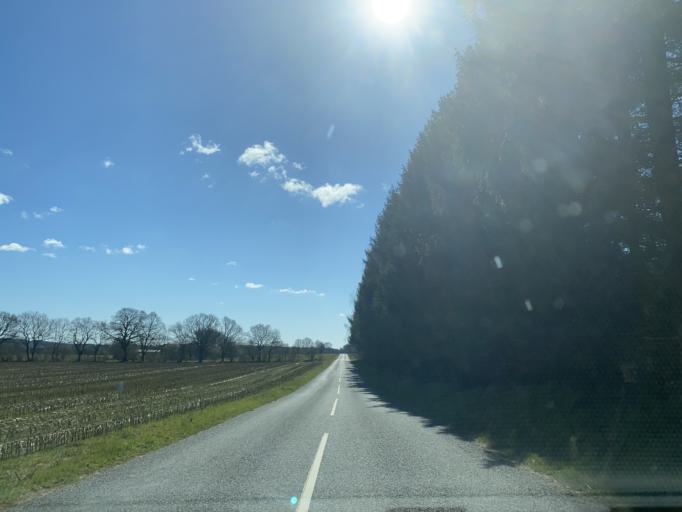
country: DK
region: Central Jutland
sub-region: Viborg Kommune
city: Bjerringbro
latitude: 56.2605
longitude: 9.6441
